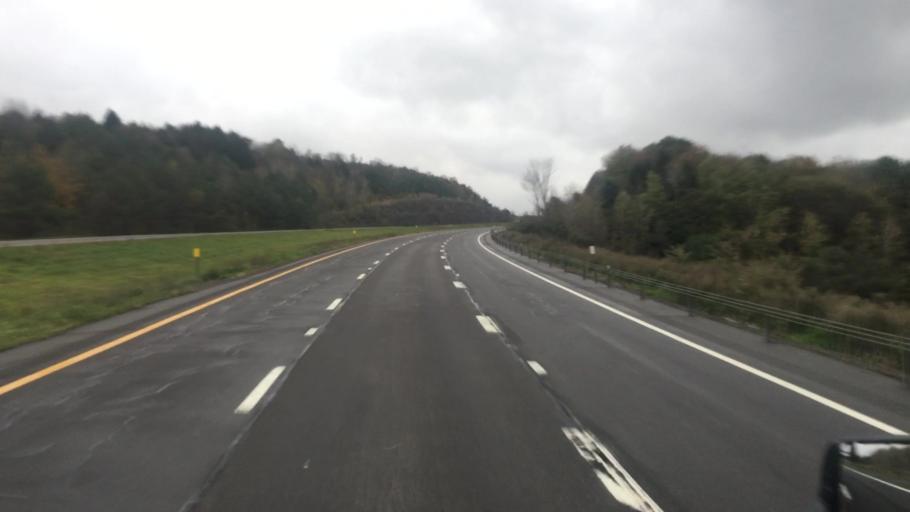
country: US
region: New York
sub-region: Chenango County
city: Greene
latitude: 42.1897
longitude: -75.6523
